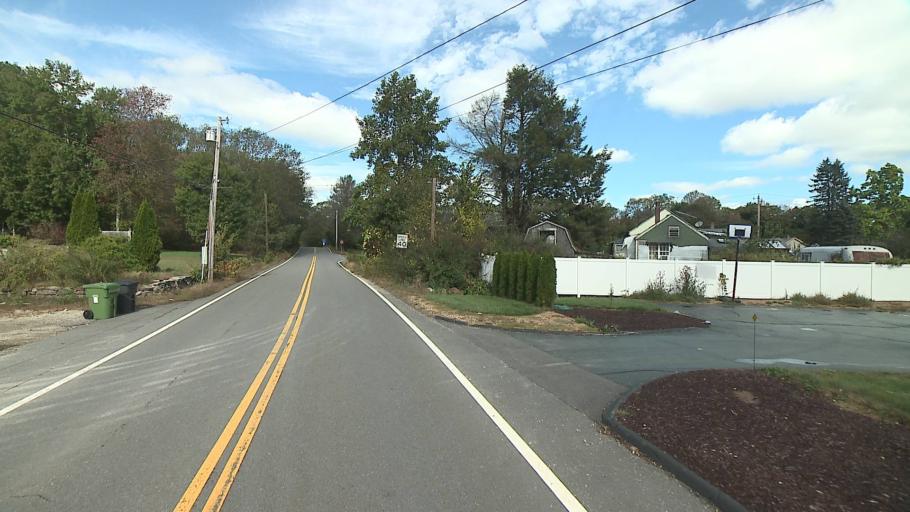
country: US
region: Massachusetts
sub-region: Worcester County
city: Webster
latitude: 42.0245
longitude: -71.8880
